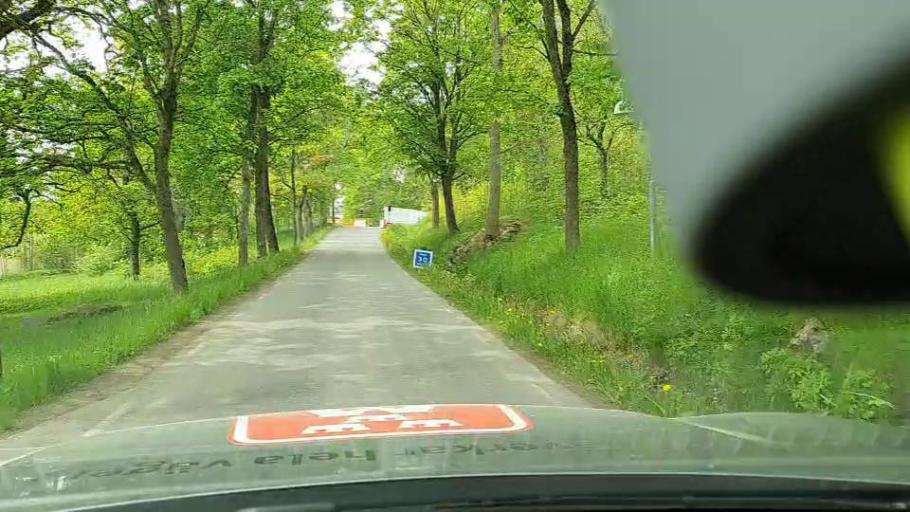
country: SE
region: Soedermanland
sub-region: Flens Kommun
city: Halleforsnas
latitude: 59.0985
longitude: 16.4894
